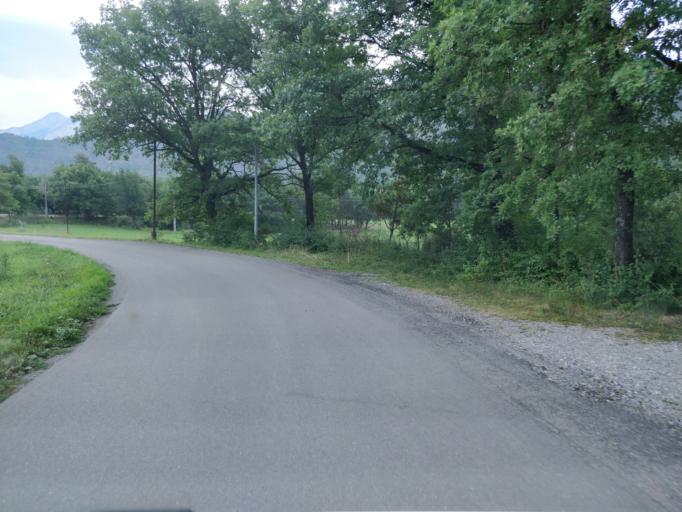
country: FR
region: Provence-Alpes-Cote d'Azur
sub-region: Departement des Alpes-de-Haute-Provence
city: Digne-les-Bains
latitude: 44.1327
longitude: 6.2492
